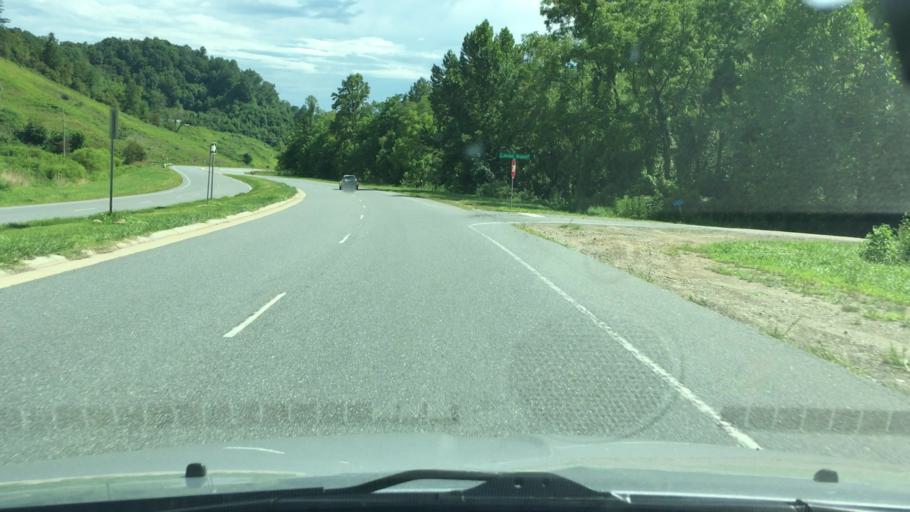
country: US
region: North Carolina
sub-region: Madison County
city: Mars Hill
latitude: 35.8787
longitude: -82.4804
